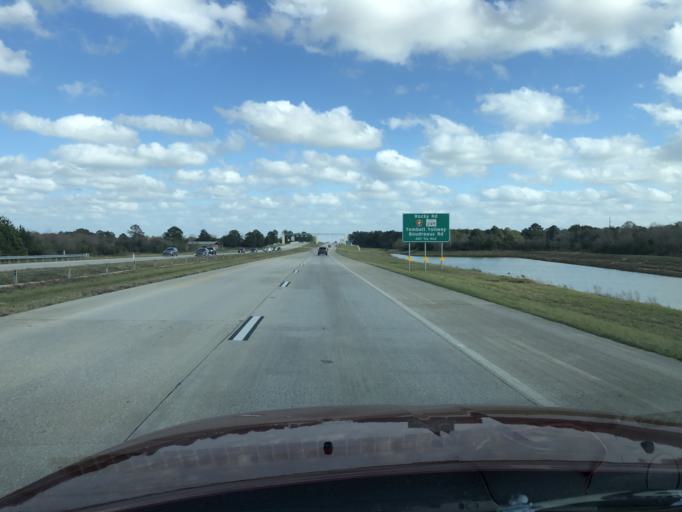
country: US
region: Texas
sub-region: Harris County
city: Tomball
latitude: 30.0519
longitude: -95.6443
